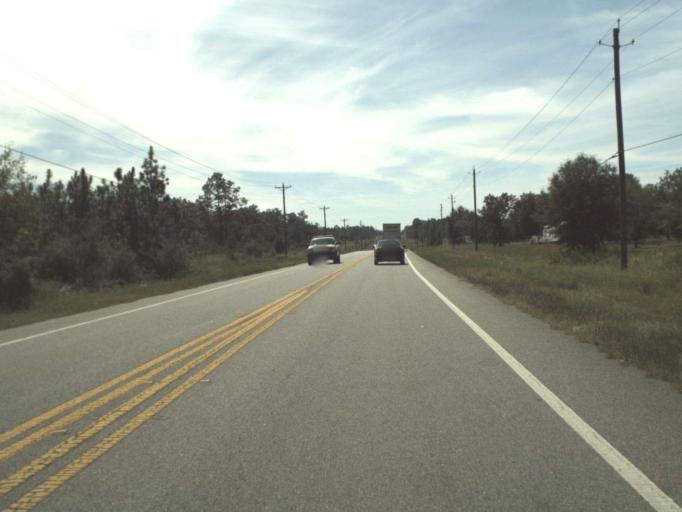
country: US
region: Florida
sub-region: Holmes County
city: Bonifay
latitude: 30.5385
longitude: -85.6383
